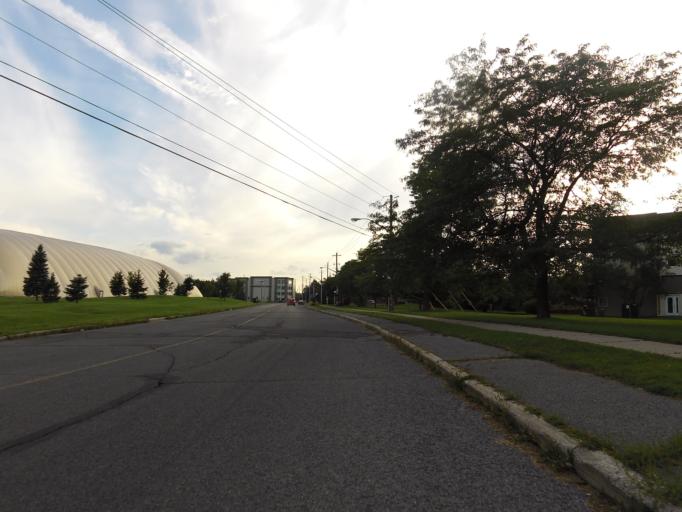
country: CA
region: Ontario
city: Bells Corners
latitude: 45.3249
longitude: -75.7750
